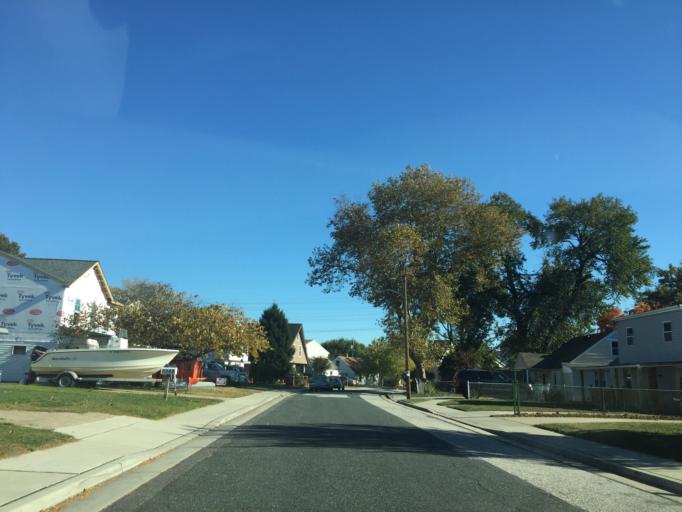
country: US
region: Maryland
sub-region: Baltimore County
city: Dundalk
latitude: 39.2498
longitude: -76.5065
